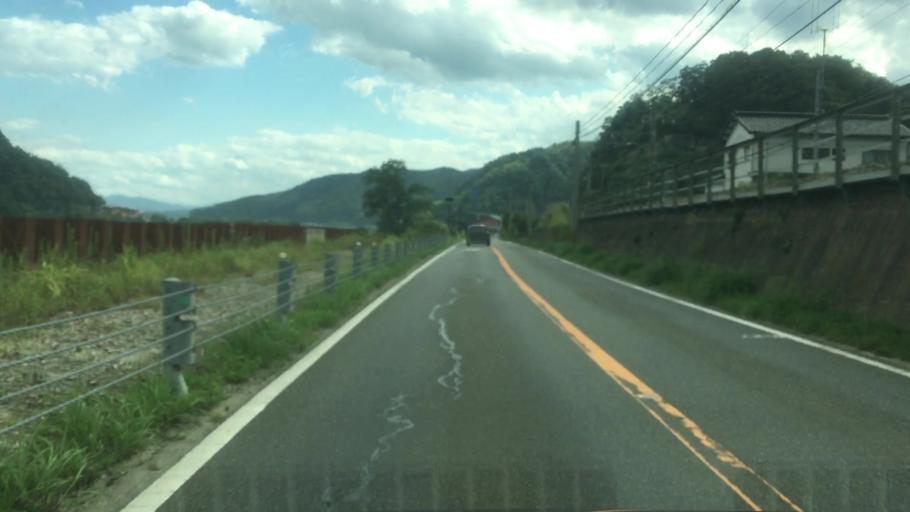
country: JP
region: Hyogo
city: Toyooka
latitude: 35.5972
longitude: 134.8017
